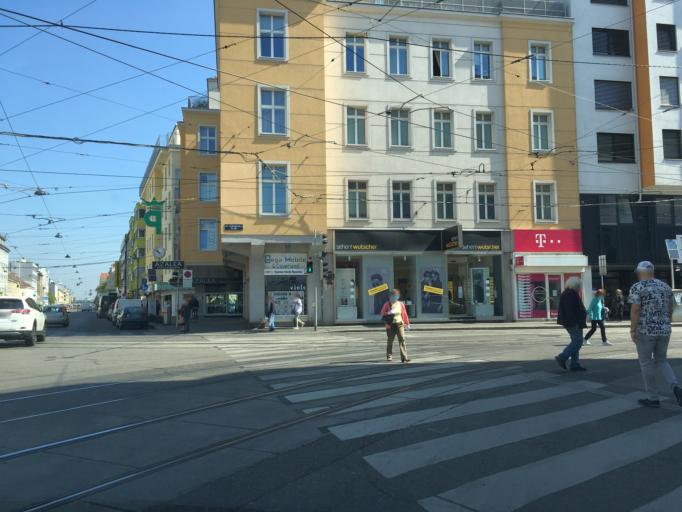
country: AT
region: Vienna
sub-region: Wien Stadt
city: Vienna
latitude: 48.2582
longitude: 16.3981
